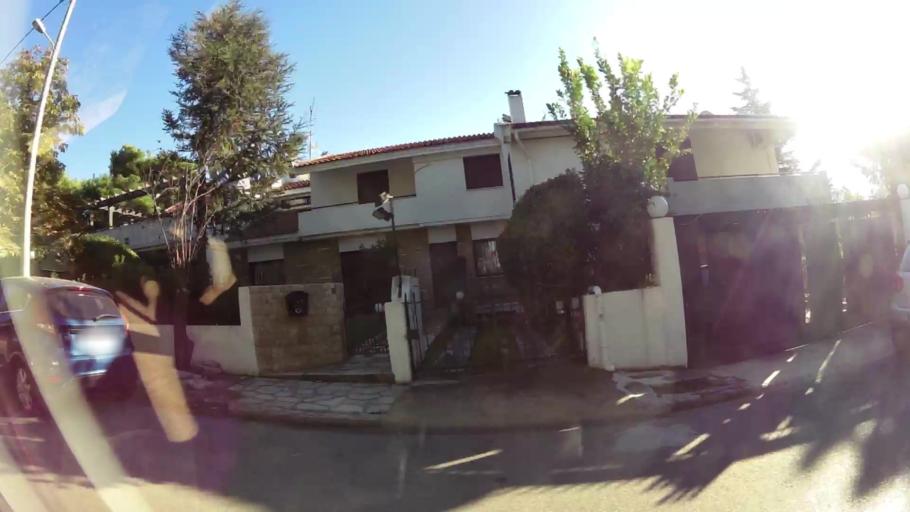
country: GR
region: Attica
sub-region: Nomarchia Athinas
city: Kifisia
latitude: 38.0854
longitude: 23.8076
